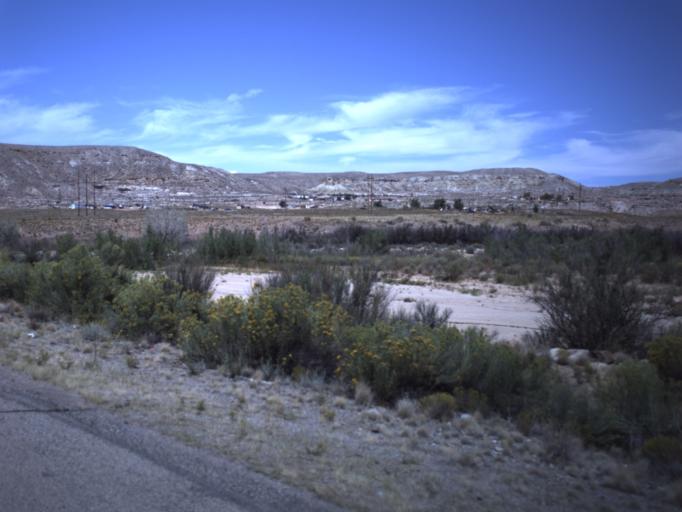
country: US
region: Utah
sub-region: San Juan County
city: Blanding
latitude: 37.2717
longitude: -109.3271
